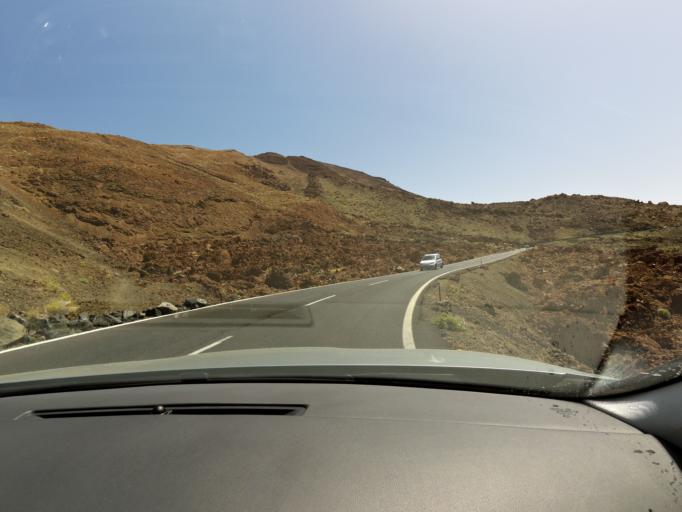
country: ES
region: Canary Islands
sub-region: Provincia de Santa Cruz de Tenerife
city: Vilaflor
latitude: 28.2581
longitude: -16.6179
